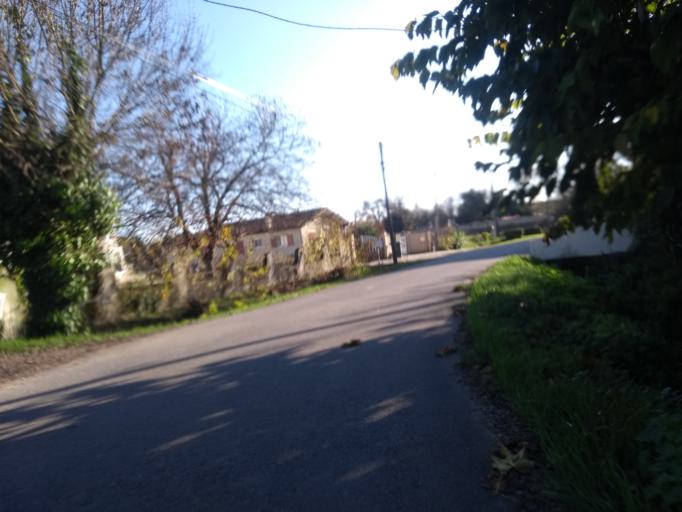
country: FR
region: Aquitaine
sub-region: Departement de la Gironde
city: Cambes
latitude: 44.7277
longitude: -0.4747
